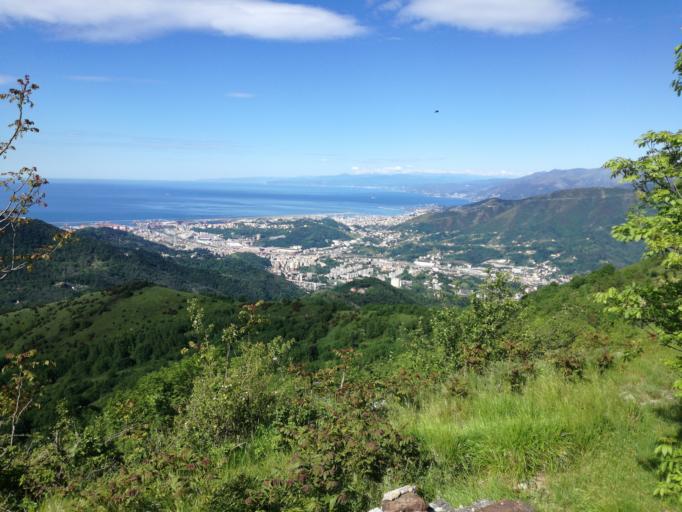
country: IT
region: Liguria
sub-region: Provincia di Genova
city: Manesseno
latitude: 44.4565
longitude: 8.9362
